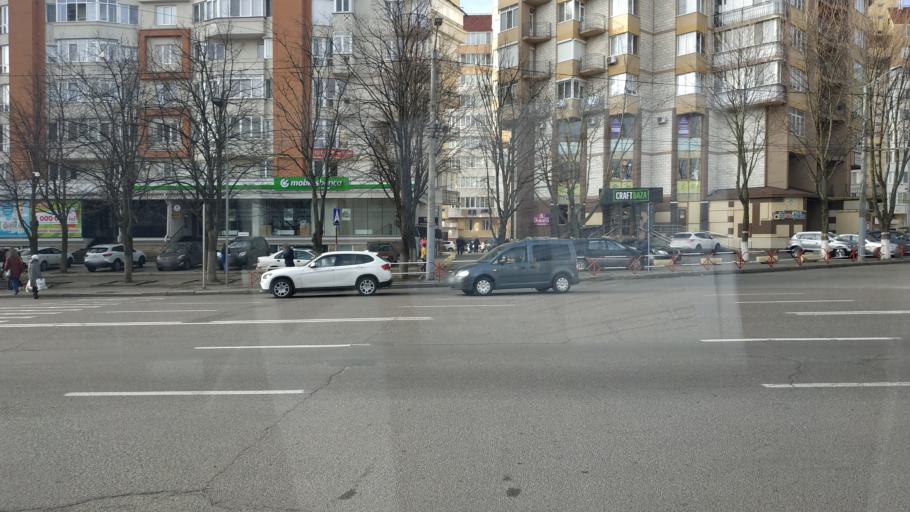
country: MD
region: Chisinau
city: Vatra
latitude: 47.0414
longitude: 28.7640
